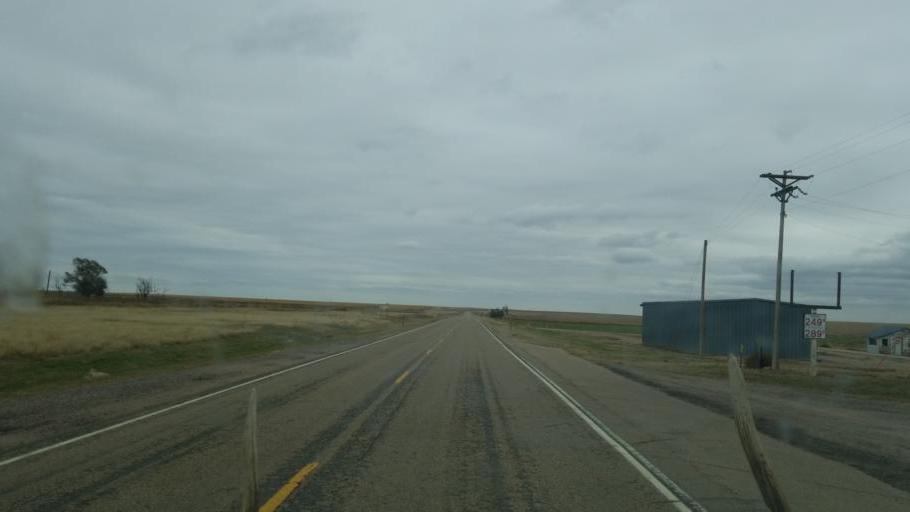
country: US
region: Colorado
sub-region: Cheyenne County
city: Cheyenne Wells
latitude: 38.8496
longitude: -102.1750
